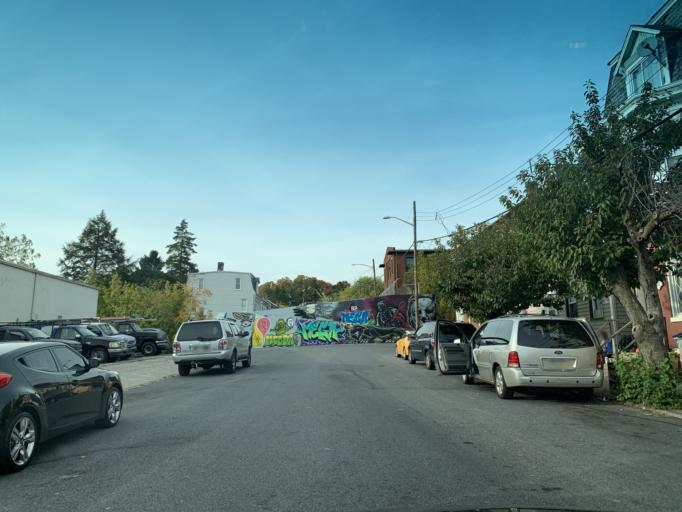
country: US
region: Pennsylvania
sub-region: York County
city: York
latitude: 39.9620
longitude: -76.7383
